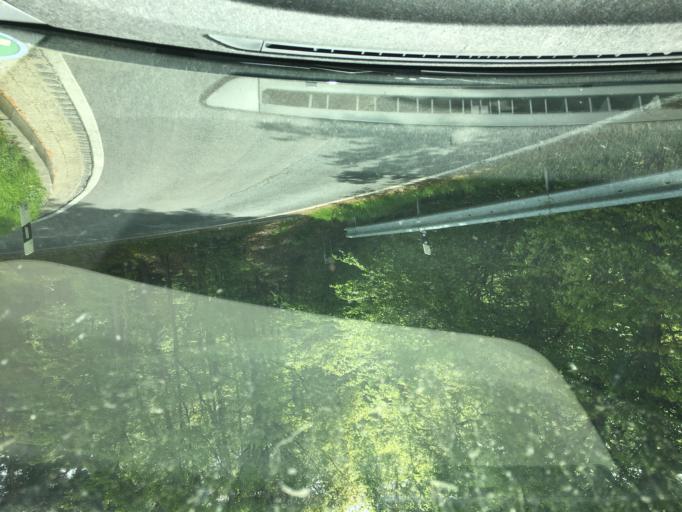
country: DE
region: Rheinland-Pfalz
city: Lind
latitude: 50.4951
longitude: 6.9199
